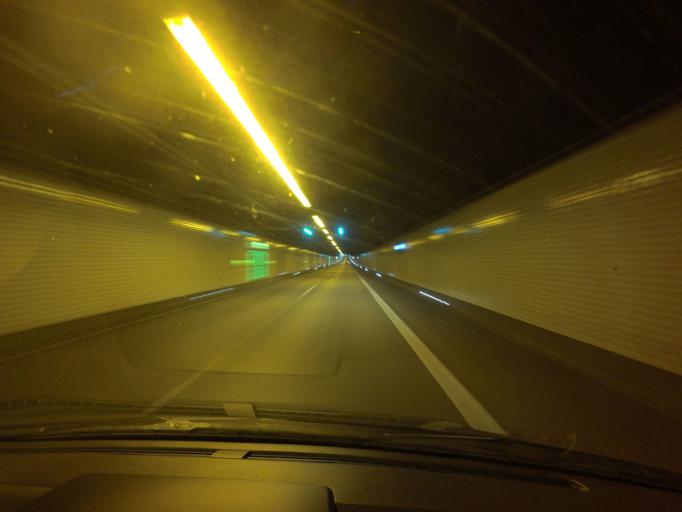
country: DE
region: Lower Saxony
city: Jemgum
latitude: 53.2345
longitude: 7.4059
